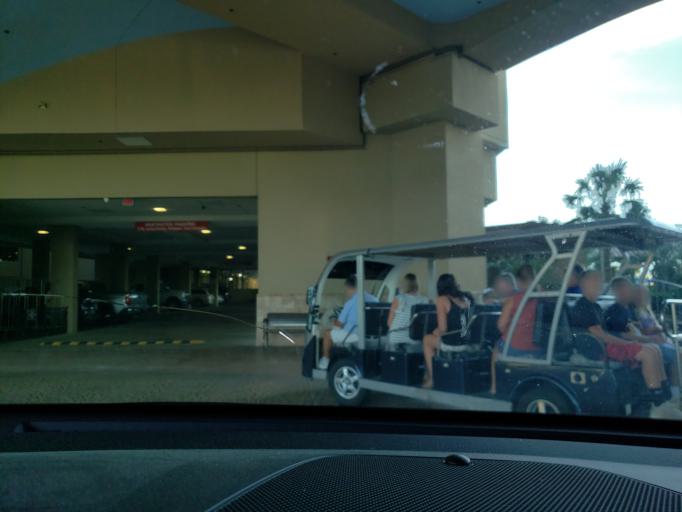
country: US
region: South Carolina
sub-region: Horry County
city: North Myrtle Beach
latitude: 33.7909
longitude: -78.7365
